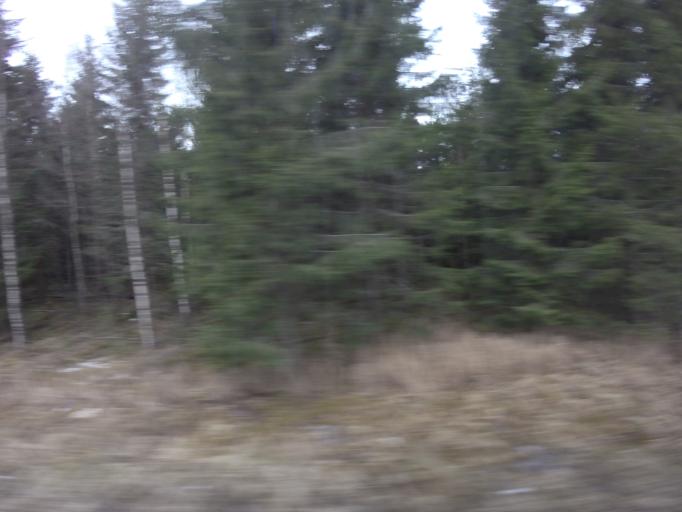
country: NO
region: Ostfold
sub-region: Trogstad
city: Skjonhaug
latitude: 59.6802
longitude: 11.3036
